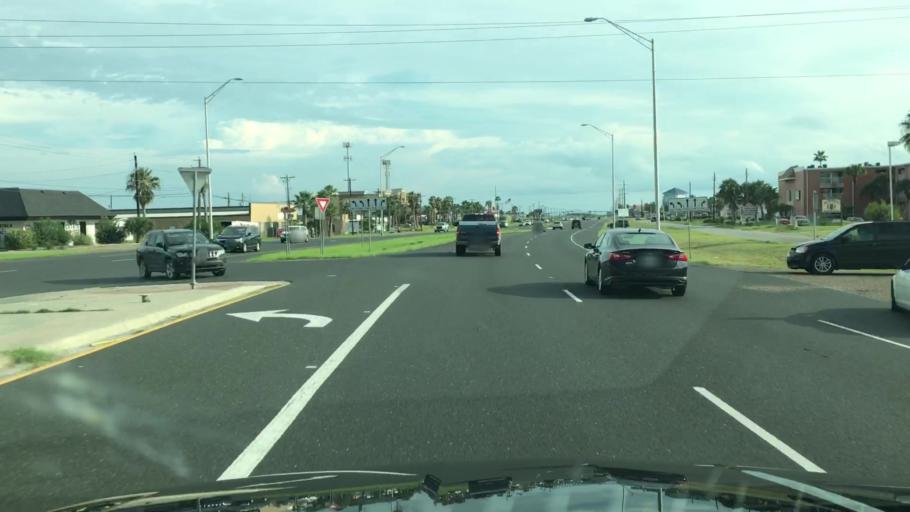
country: US
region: Texas
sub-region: Nueces County
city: Corpus Christi
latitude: 27.6239
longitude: -97.2218
